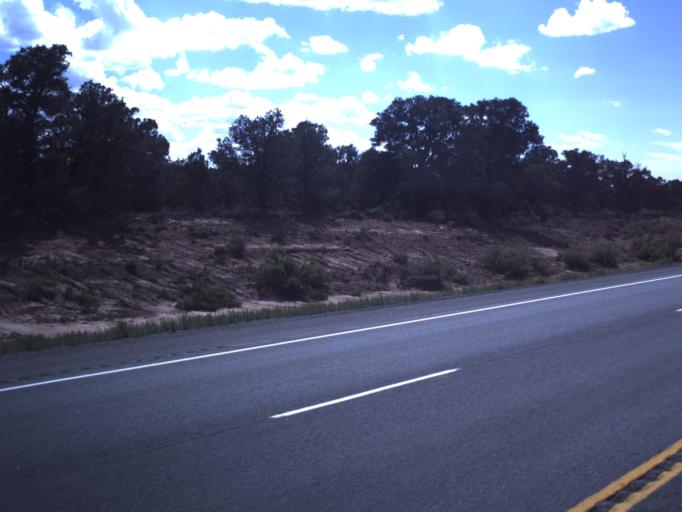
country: US
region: Utah
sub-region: Duchesne County
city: Duchesne
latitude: 40.2004
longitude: -110.7007
